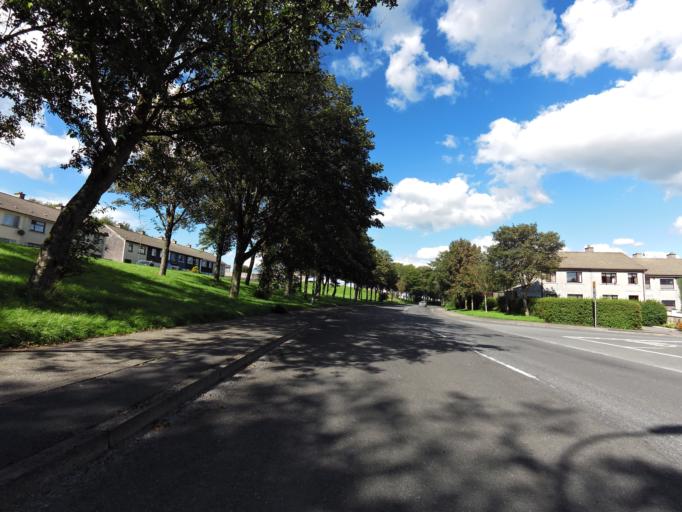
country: IE
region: Connaught
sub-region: County Galway
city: Gaillimh
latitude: 53.2800
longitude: -9.0772
